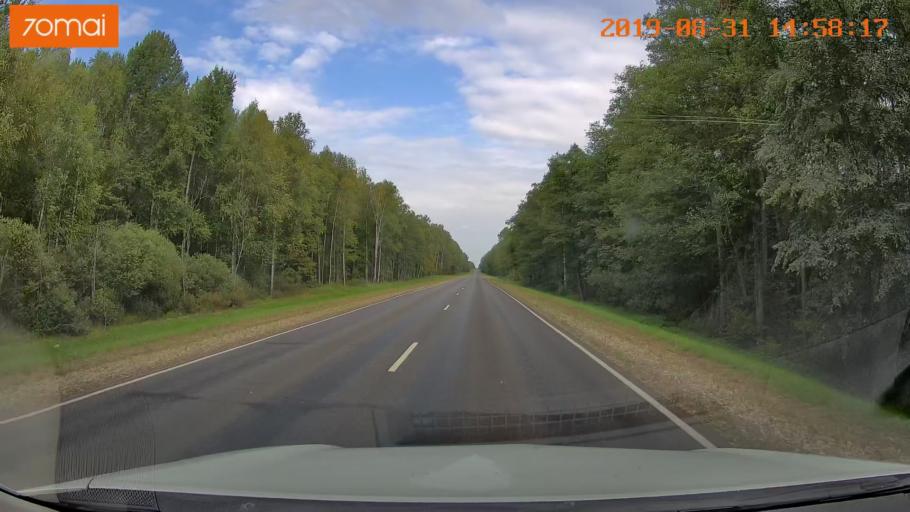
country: RU
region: Kaluga
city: Spas-Demensk
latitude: 54.3164
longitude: 33.9778
